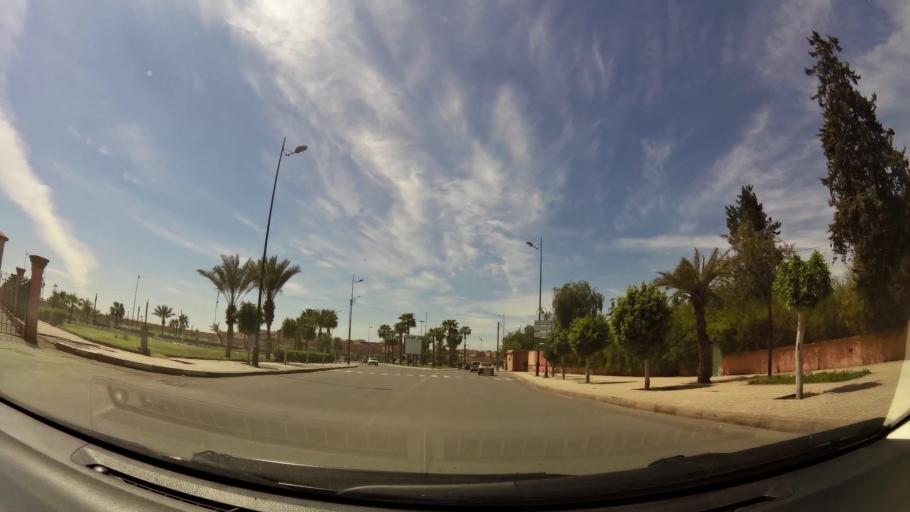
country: MA
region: Marrakech-Tensift-Al Haouz
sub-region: Marrakech
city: Marrakesh
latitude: 31.6143
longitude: -7.9737
